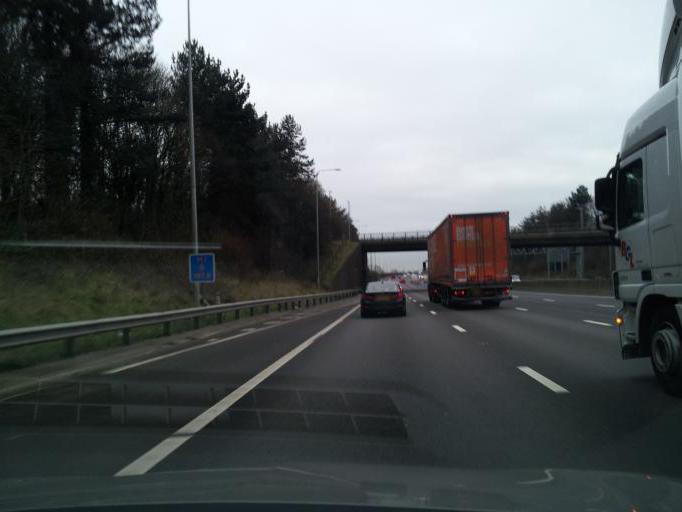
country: GB
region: England
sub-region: Nottinghamshire
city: Kimberley
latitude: 52.9493
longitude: -1.2776
